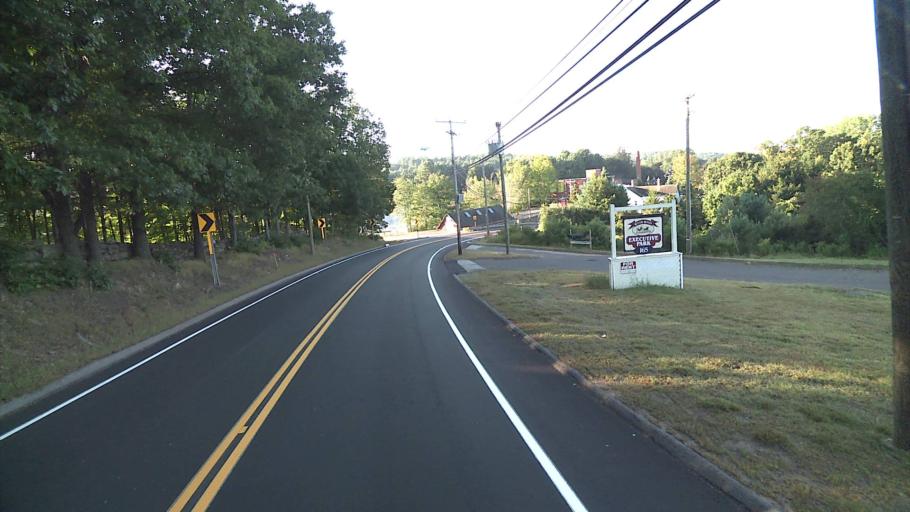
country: US
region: Connecticut
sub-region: Tolland County
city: Tolland
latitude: 41.8583
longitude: -72.2996
